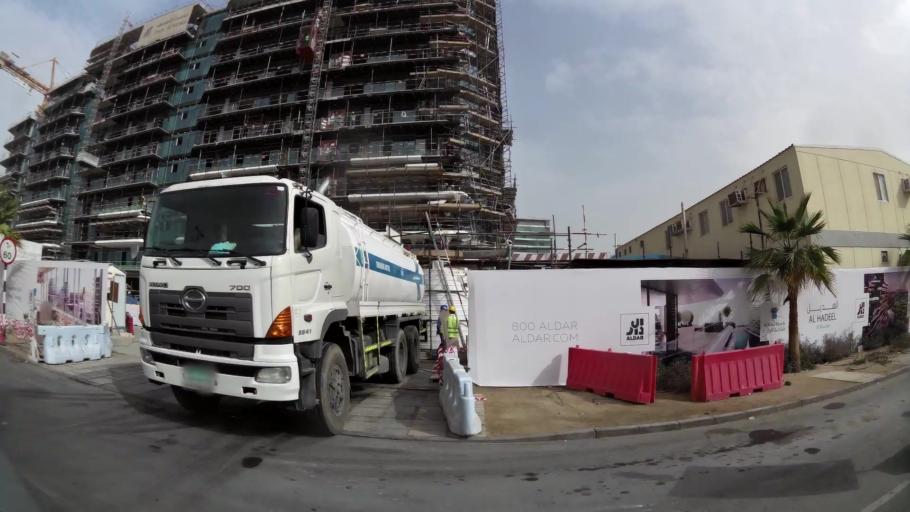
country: AE
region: Abu Dhabi
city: Abu Dhabi
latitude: 24.4483
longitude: 54.6001
